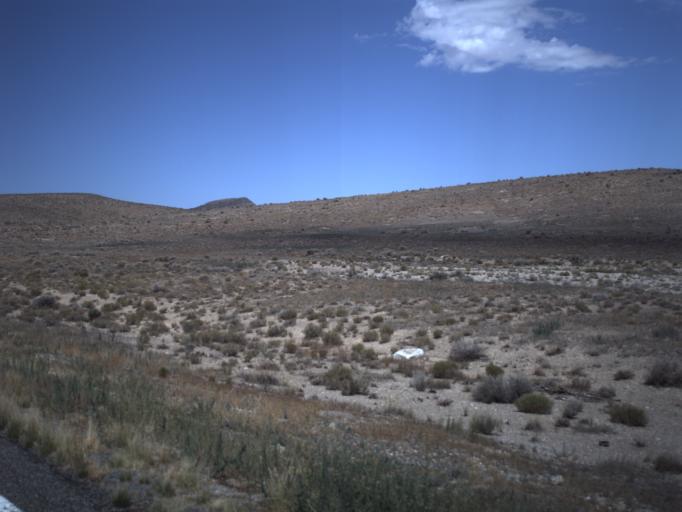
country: US
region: Utah
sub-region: Beaver County
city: Milford
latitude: 39.0364
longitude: -113.3355
